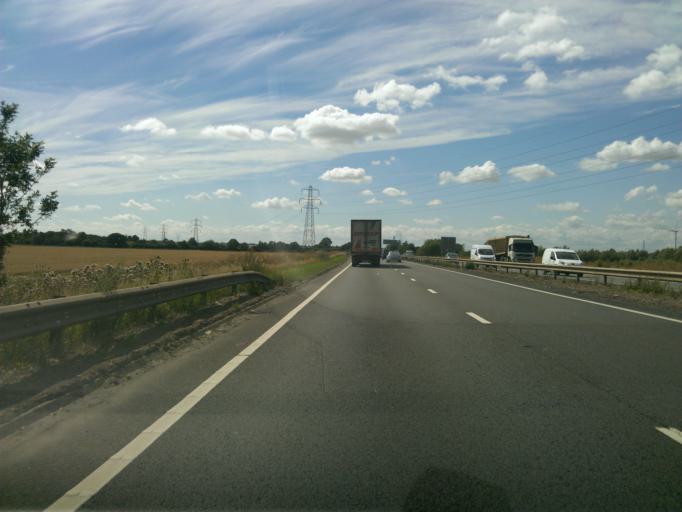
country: GB
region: England
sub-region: Cambridgeshire
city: Buckden
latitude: 52.3322
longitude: -0.2640
